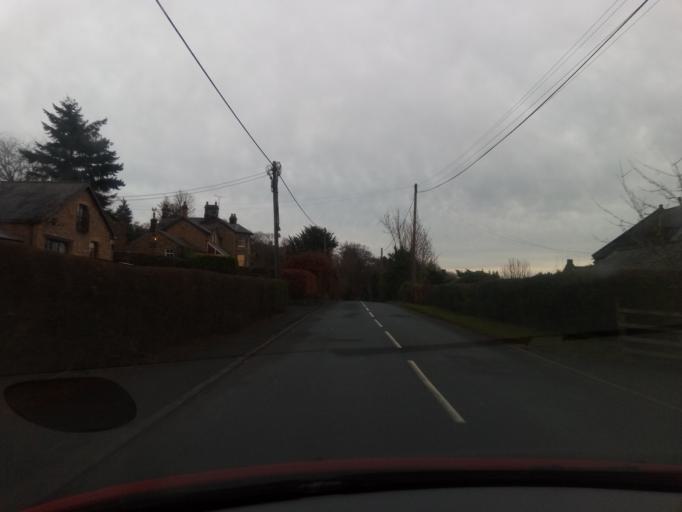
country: GB
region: England
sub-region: Northumberland
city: Whittingham
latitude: 55.4684
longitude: -1.8276
